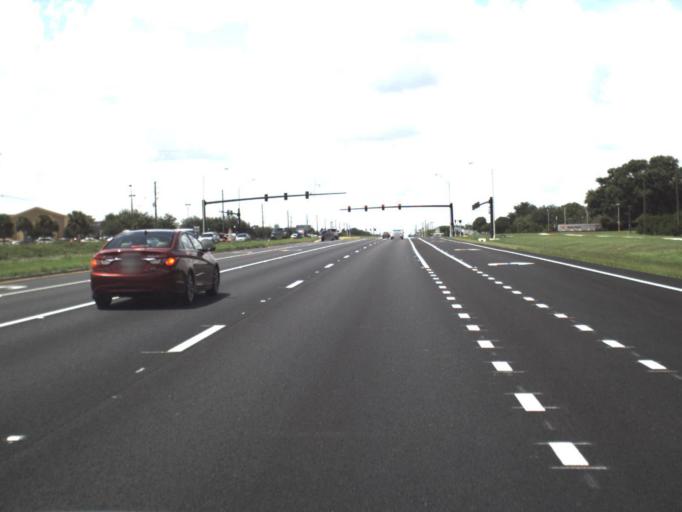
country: US
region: Florida
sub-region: Polk County
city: Cypress Gardens
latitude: 27.9787
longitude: -81.6458
